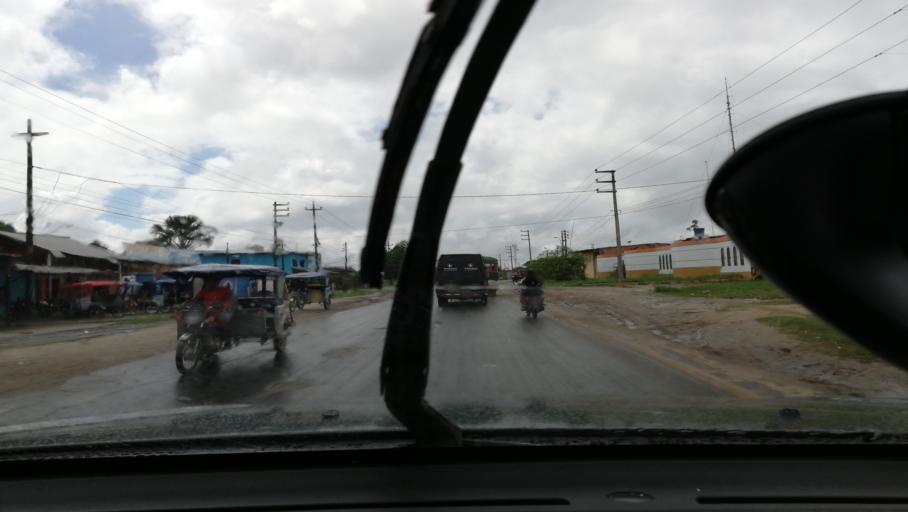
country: PE
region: Loreto
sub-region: Provincia de Maynas
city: Iquitos
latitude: -3.7992
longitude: -73.3063
